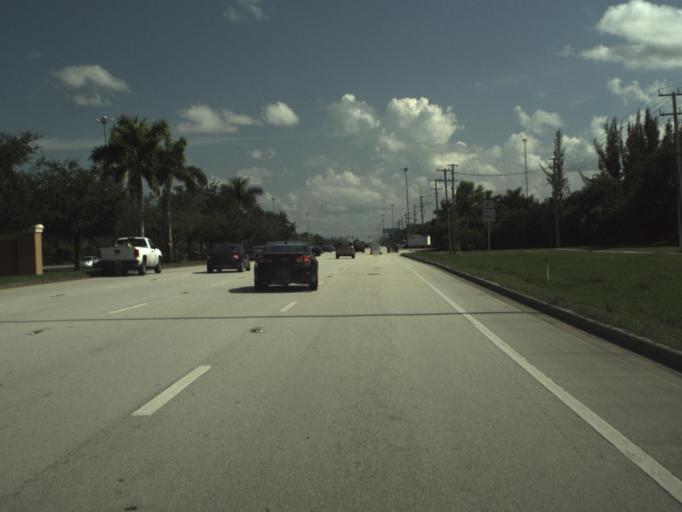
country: US
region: Florida
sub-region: Palm Beach County
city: Wellington
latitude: 26.6227
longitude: -80.2048
